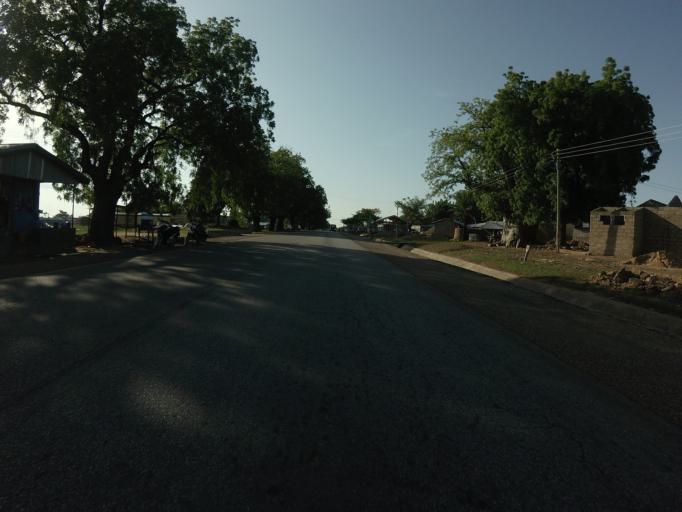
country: GH
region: Upper East
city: Navrongo
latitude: 10.9662
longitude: -1.1011
